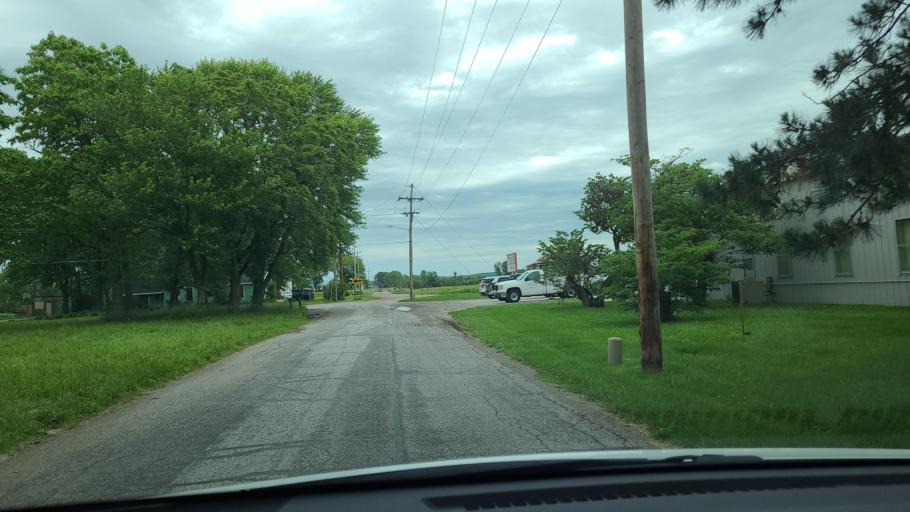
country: US
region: Kansas
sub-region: Douglas County
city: Lawrence
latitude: 38.9817
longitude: -95.2145
